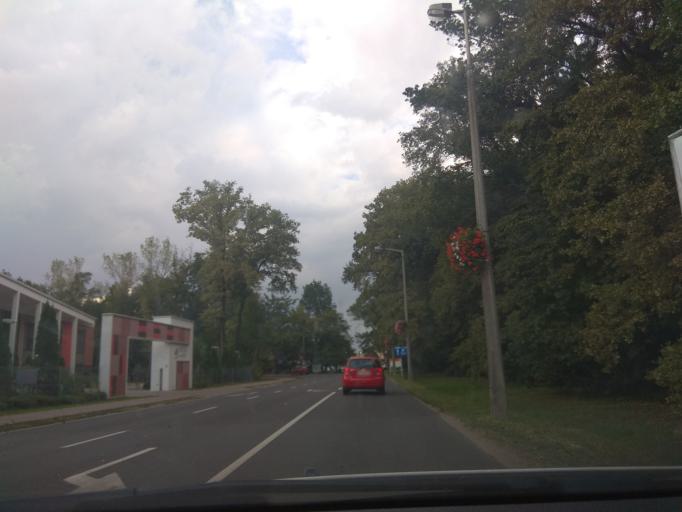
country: HU
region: Borsod-Abauj-Zemplen
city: Sajooeroes
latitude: 47.9257
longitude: 21.0428
